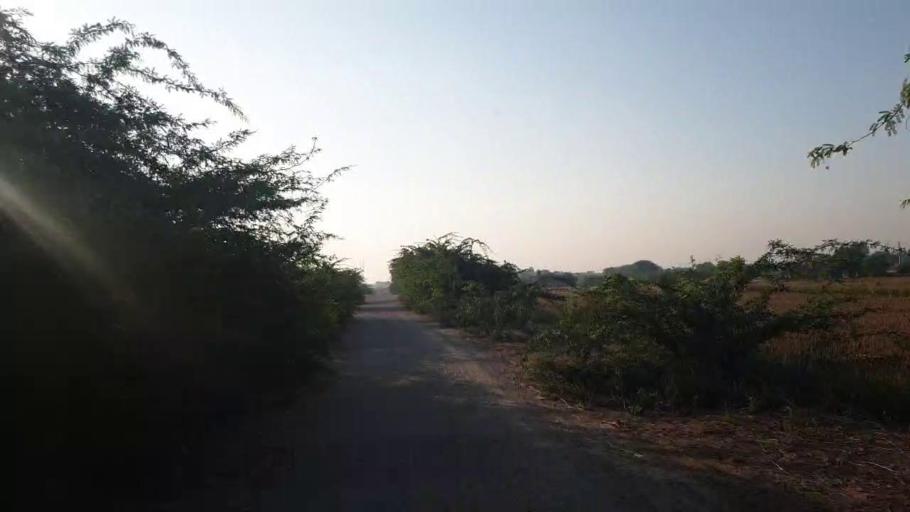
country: PK
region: Sindh
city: Badin
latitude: 24.6568
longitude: 68.7882
